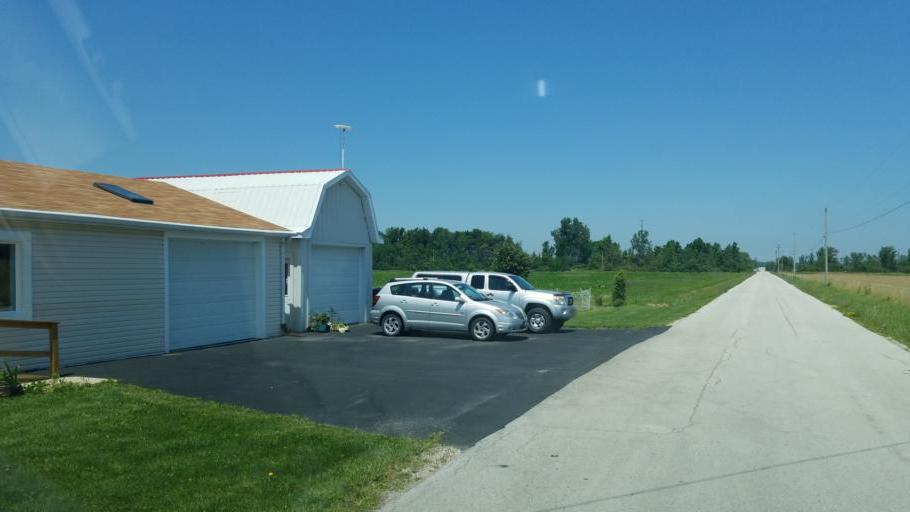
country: US
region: Ohio
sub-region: Sandusky County
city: Clyde
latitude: 41.3675
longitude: -82.9929
